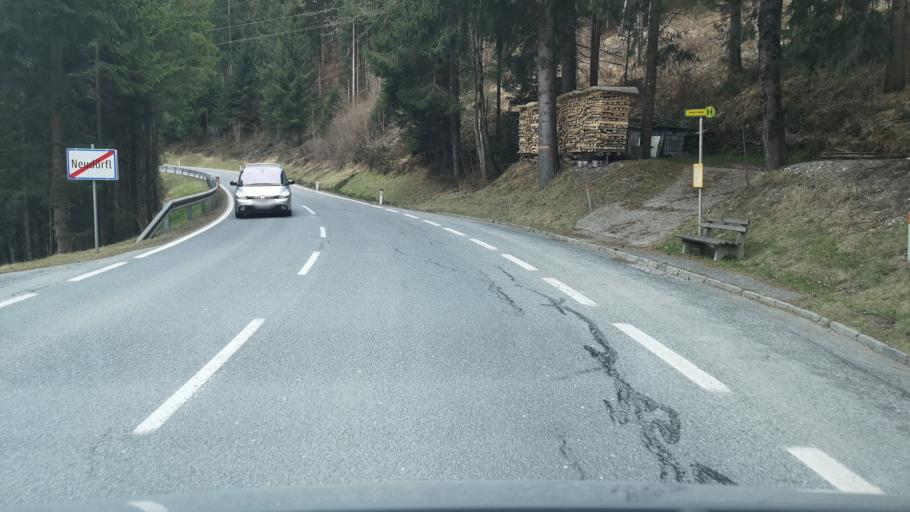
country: AT
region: Styria
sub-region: Politischer Bezirk Weiz
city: Birkfeld
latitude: 47.3436
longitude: 15.6976
